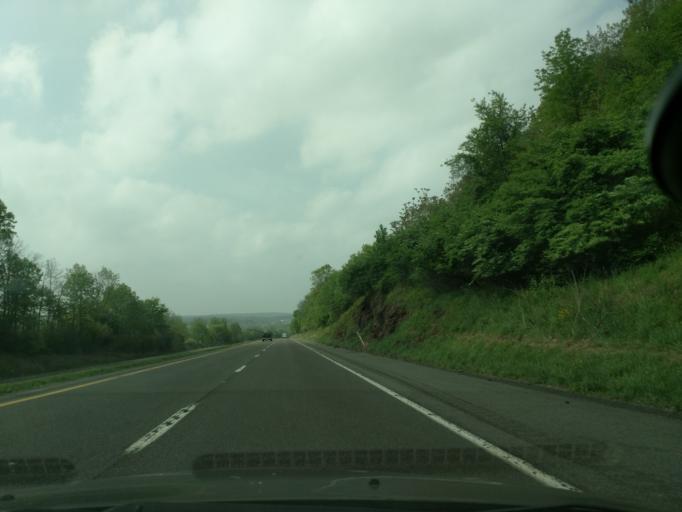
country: US
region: Pennsylvania
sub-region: Berks County
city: Flying Hills
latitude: 40.2285
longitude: -75.9127
